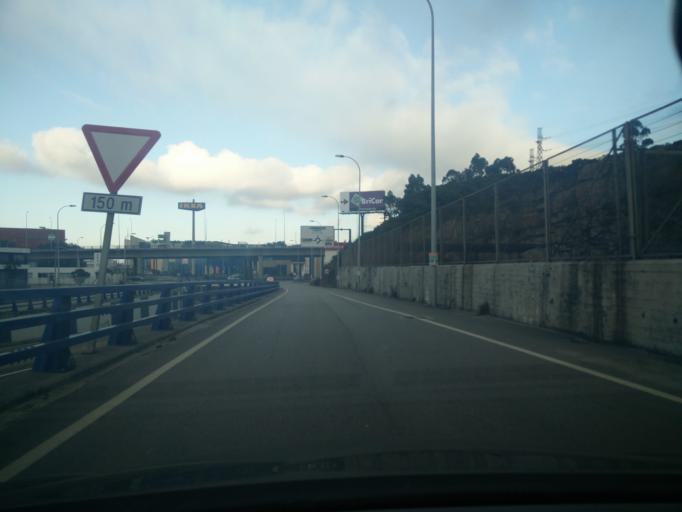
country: ES
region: Galicia
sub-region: Provincia da Coruna
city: A Coruna
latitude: 43.3445
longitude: -8.4354
